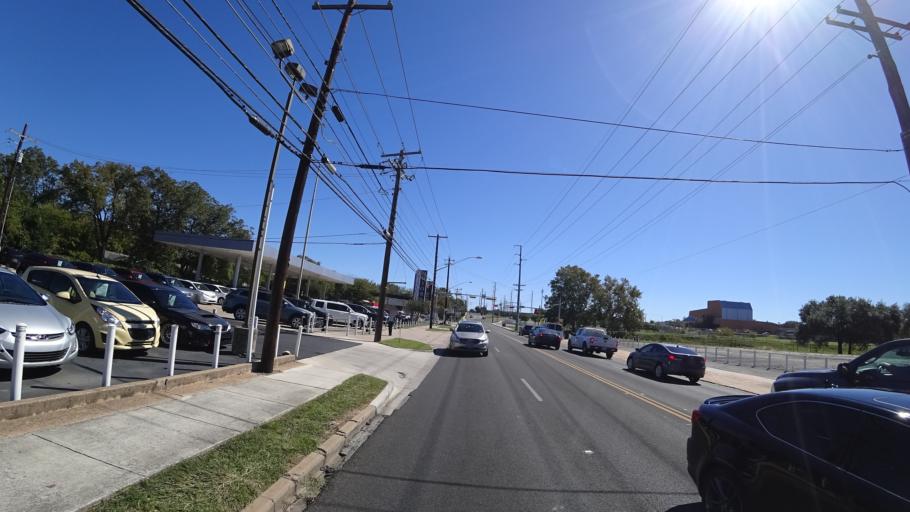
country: US
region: Texas
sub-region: Travis County
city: Austin
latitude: 30.3302
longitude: -97.7301
